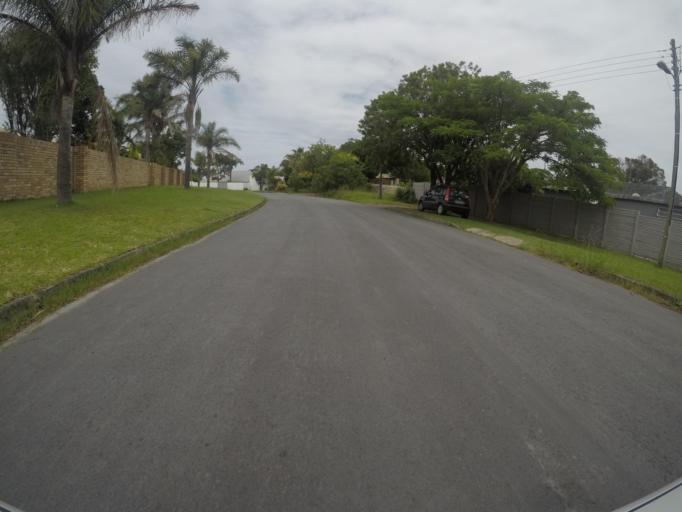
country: ZA
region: Eastern Cape
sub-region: Buffalo City Metropolitan Municipality
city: East London
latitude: -32.9641
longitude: 27.9301
